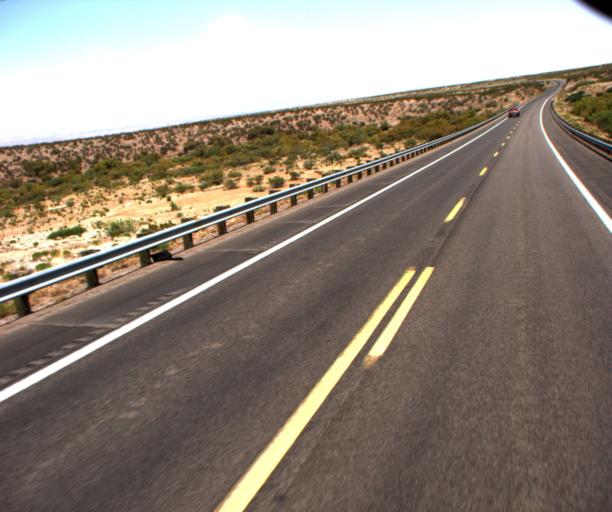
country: US
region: Arizona
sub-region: Greenlee County
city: Clifton
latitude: 32.7266
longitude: -109.1766
